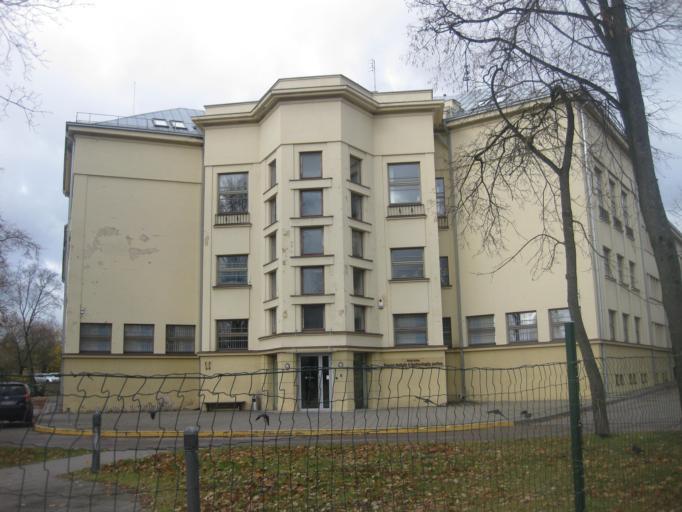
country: LT
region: Kauno apskritis
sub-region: Kaunas
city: Eiguliai
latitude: 54.9053
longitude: 23.9318
